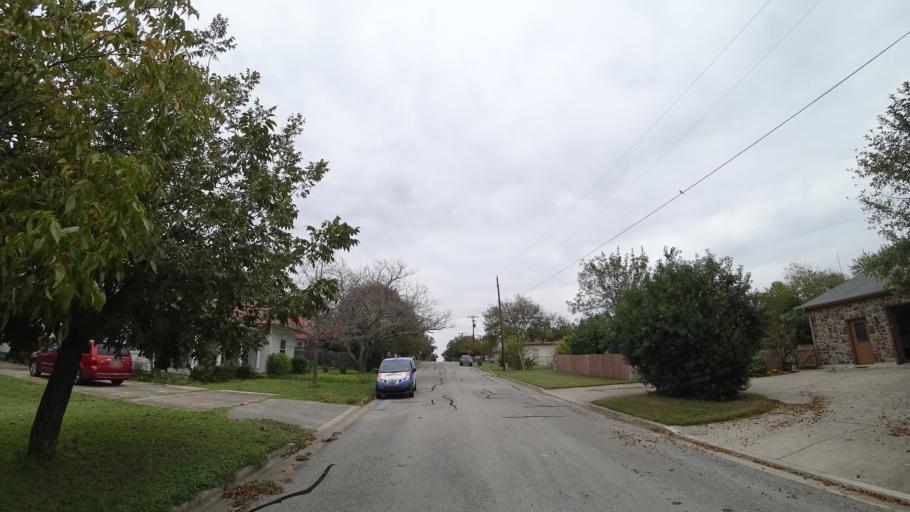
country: US
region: Texas
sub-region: Travis County
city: Pflugerville
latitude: 30.4360
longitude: -97.6233
